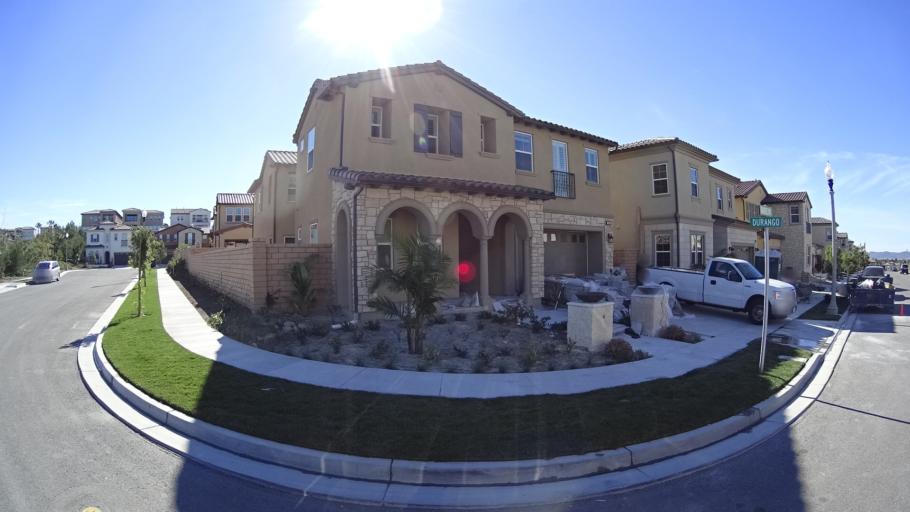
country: US
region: California
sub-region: Orange County
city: Foothill Ranch
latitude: 33.6724
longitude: -117.6801
